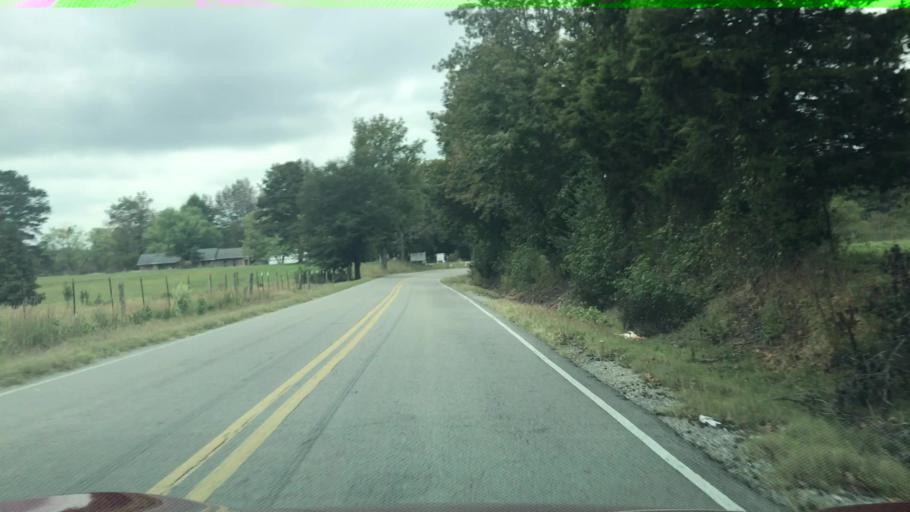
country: US
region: Alabama
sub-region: Cullman County
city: Good Hope
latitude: 34.0955
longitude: -87.0447
